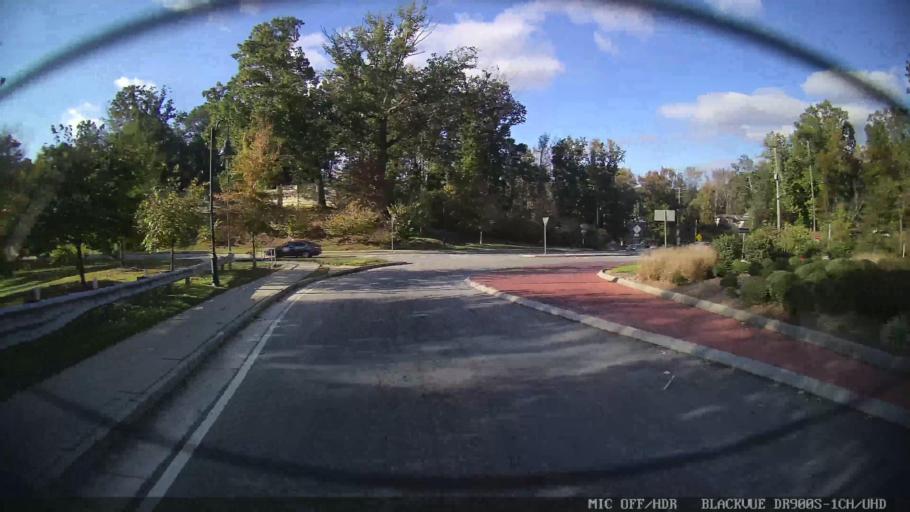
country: US
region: Georgia
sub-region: Fulton County
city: Sandy Springs
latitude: 33.9155
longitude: -84.3939
